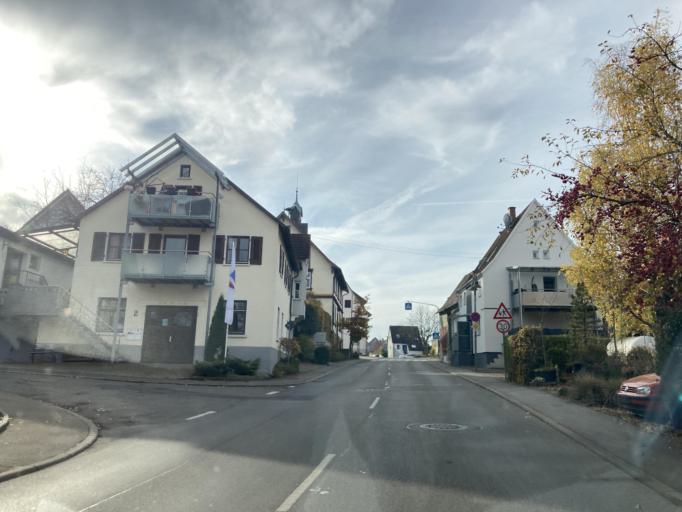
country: DE
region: Baden-Wuerttemberg
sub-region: Regierungsbezirk Stuttgart
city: Bondorf
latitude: 48.5280
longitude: 8.8687
